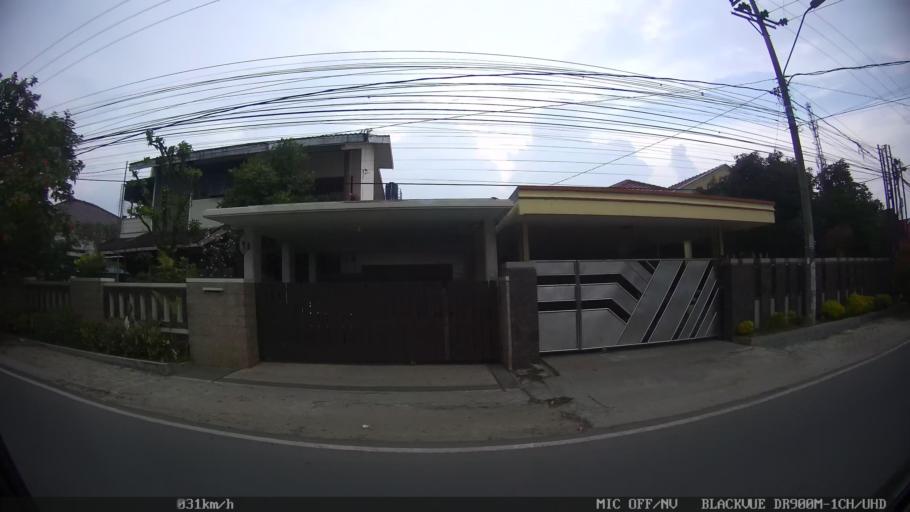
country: ID
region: Lampung
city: Kedaton
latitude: -5.4020
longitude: 105.2772
